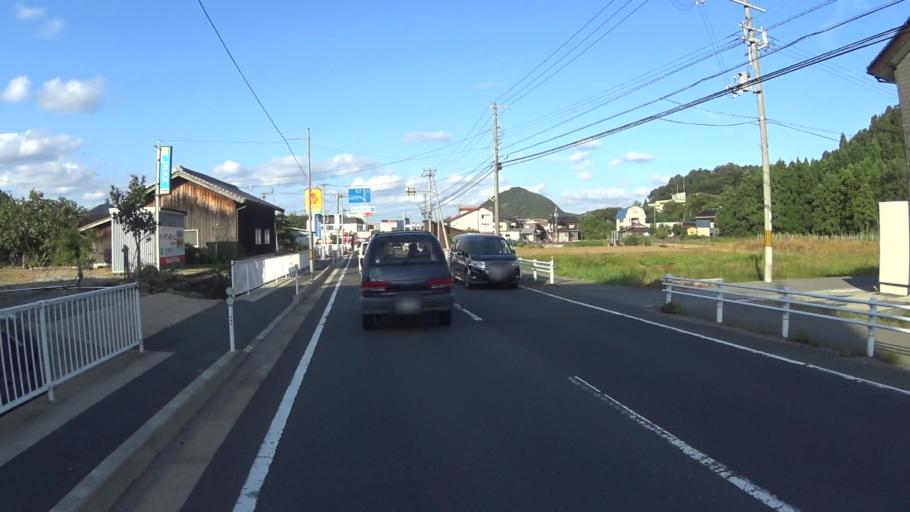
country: JP
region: Hyogo
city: Toyooka
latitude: 35.5894
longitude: 134.8708
